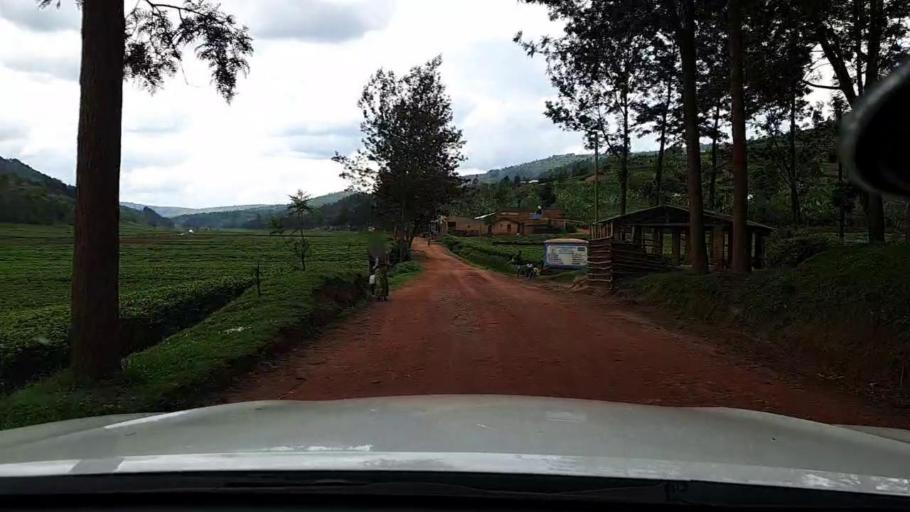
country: RW
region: Northern Province
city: Byumba
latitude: -1.6659
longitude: 29.9198
